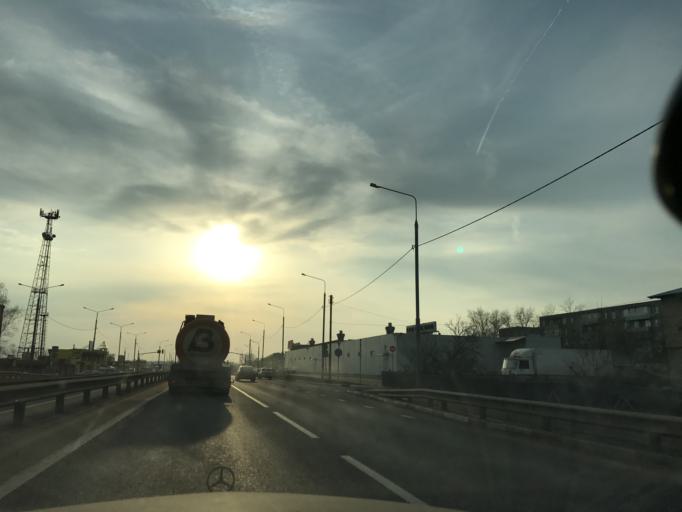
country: RU
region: Vladimir
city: Lakinsk
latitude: 56.0213
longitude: 39.9784
